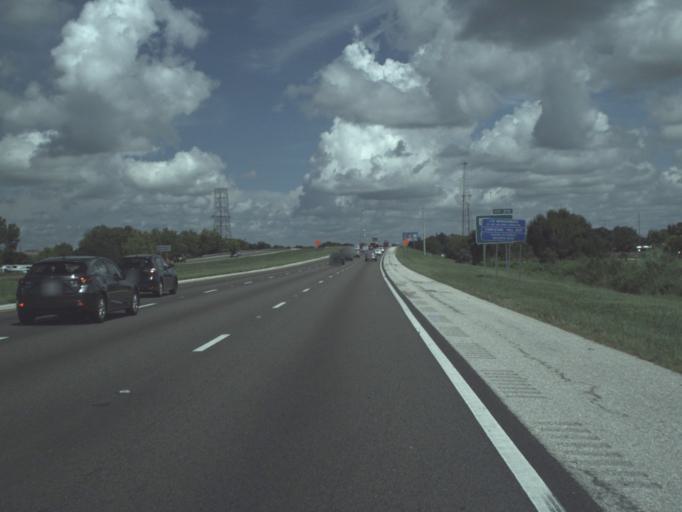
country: US
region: Florida
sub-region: Sarasota County
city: Fruitville
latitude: 27.3214
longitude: -82.4476
